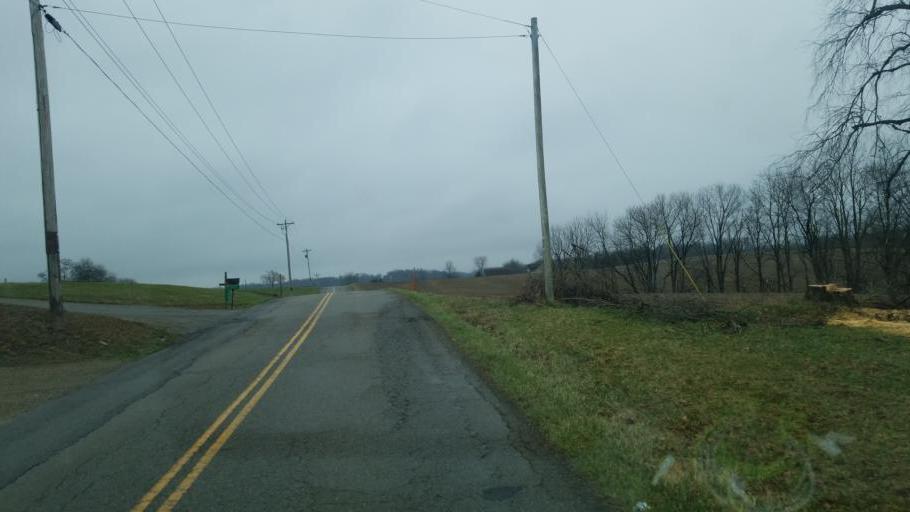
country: US
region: Ohio
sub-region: Knox County
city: Fredericktown
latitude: 40.4729
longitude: -82.4714
